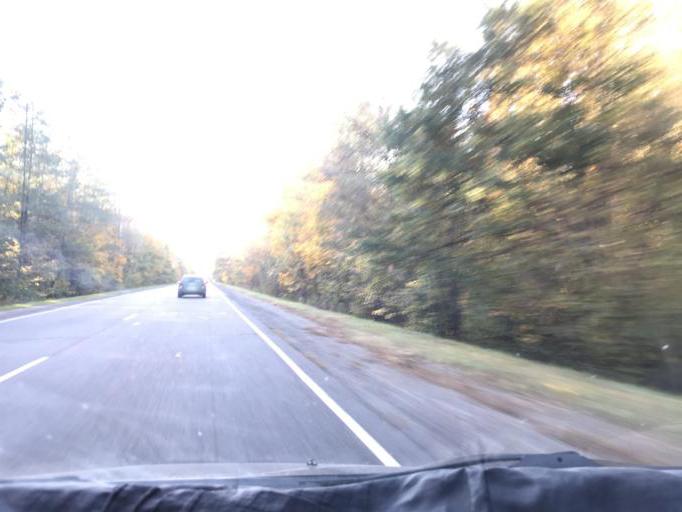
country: BY
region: Gomel
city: Pyetrykaw
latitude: 52.2669
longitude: 28.2965
